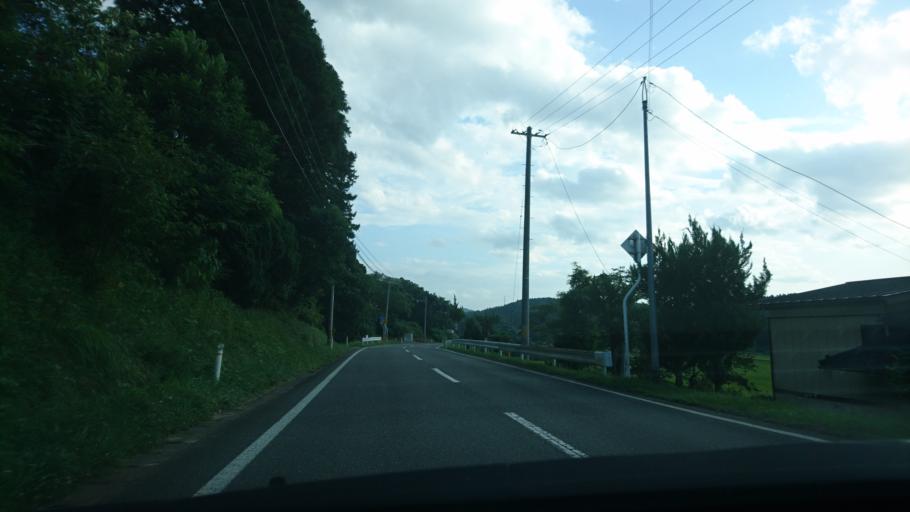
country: JP
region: Iwate
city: Ichinoseki
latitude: 39.0248
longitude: 141.2919
